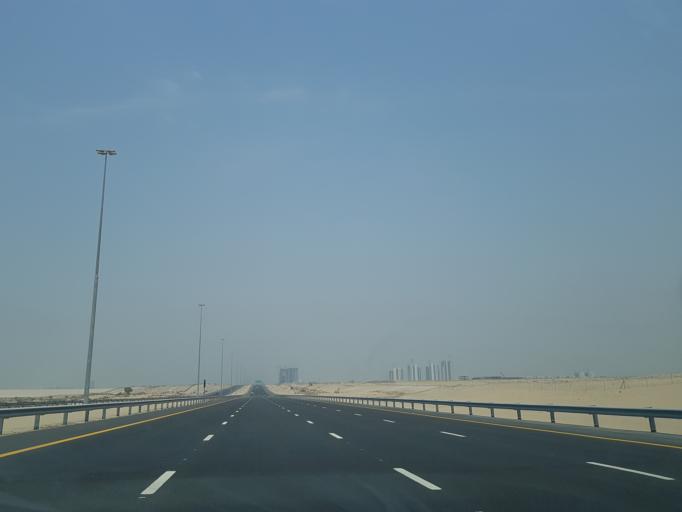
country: AE
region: Dubai
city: Dubai
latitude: 25.0141
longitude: 55.2217
